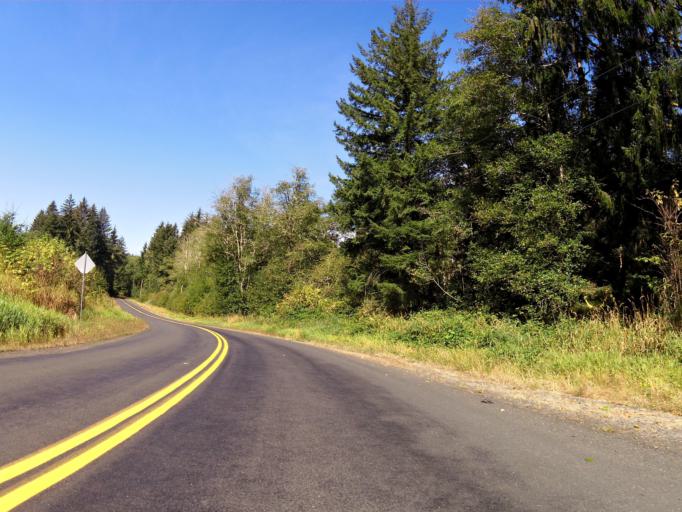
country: US
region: Washington
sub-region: Wahkiakum County
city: Cathlamet
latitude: 46.1771
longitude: -123.5281
